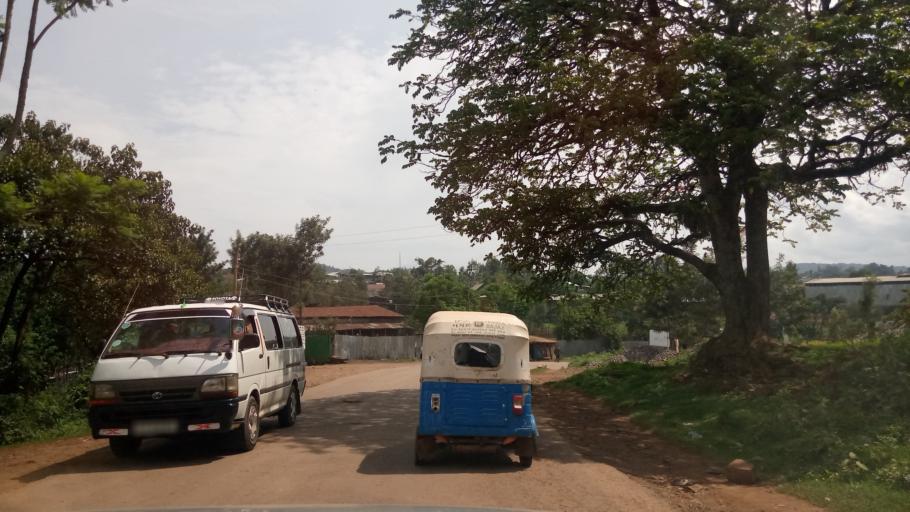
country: ET
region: Oromiya
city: Agaro
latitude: 7.8534
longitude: 36.5941
